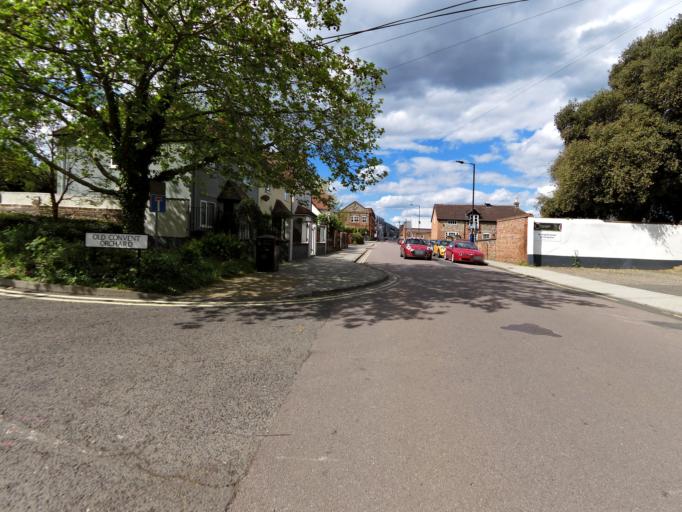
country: GB
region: England
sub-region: Suffolk
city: Bury St Edmunds
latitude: 52.2431
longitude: 0.7112
